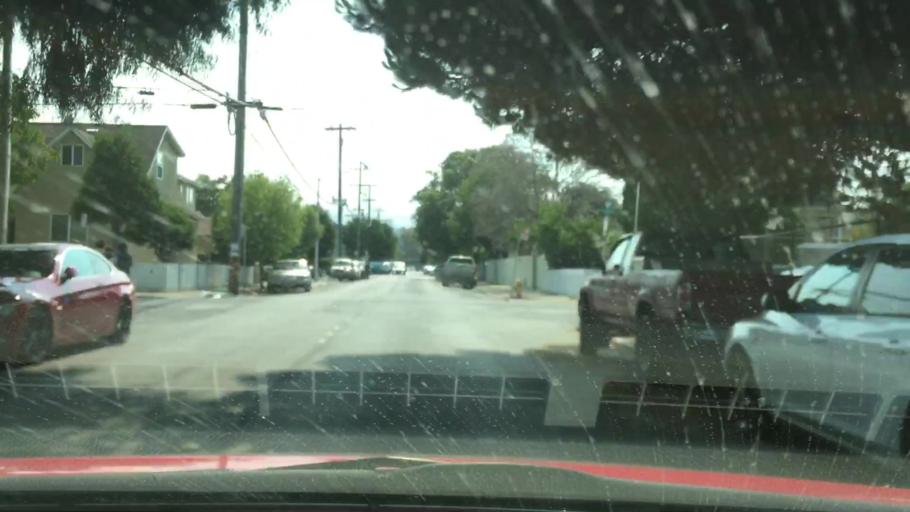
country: US
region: California
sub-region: San Mateo County
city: San Mateo
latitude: 37.5717
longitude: -122.3234
